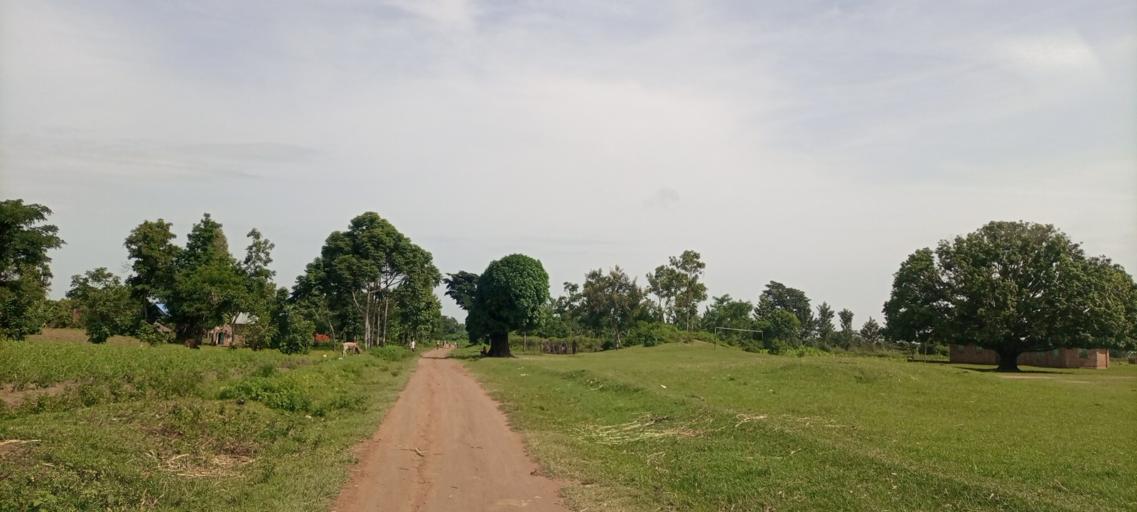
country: UG
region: Eastern Region
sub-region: Budaka District
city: Budaka
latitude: 1.1349
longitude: 34.0184
